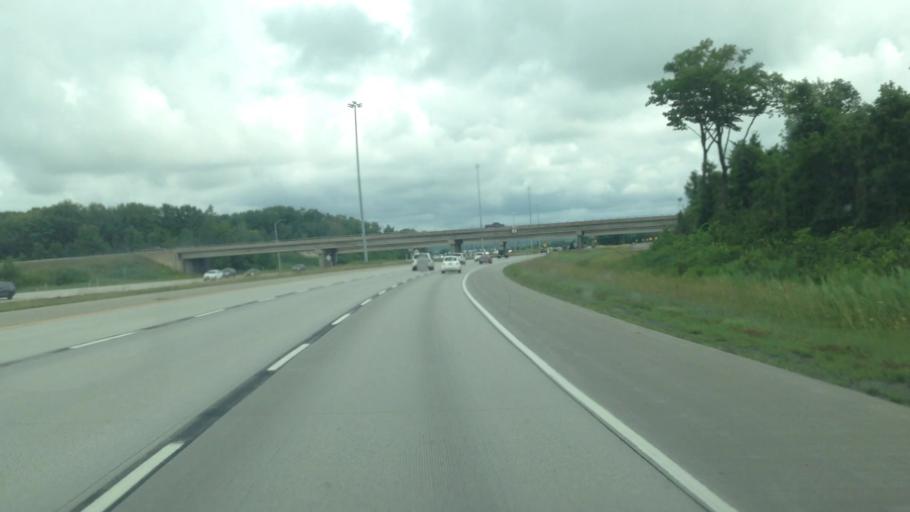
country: CA
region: Quebec
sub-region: Laurentides
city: Saint-Jerome
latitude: 45.7173
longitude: -73.9705
